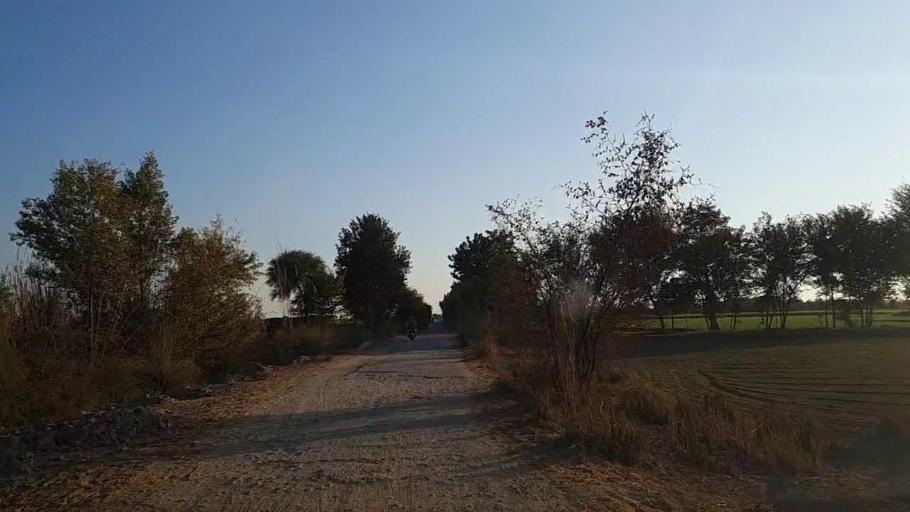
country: PK
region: Sindh
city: Khadro
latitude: 26.2762
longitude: 68.8100
